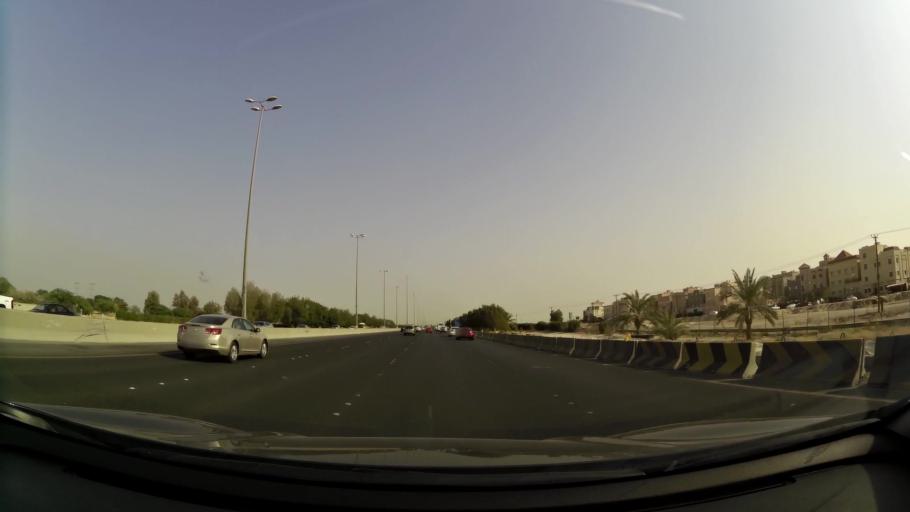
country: KW
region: Muhafazat al Jahra'
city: Al Jahra'
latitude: 29.3281
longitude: 47.7410
